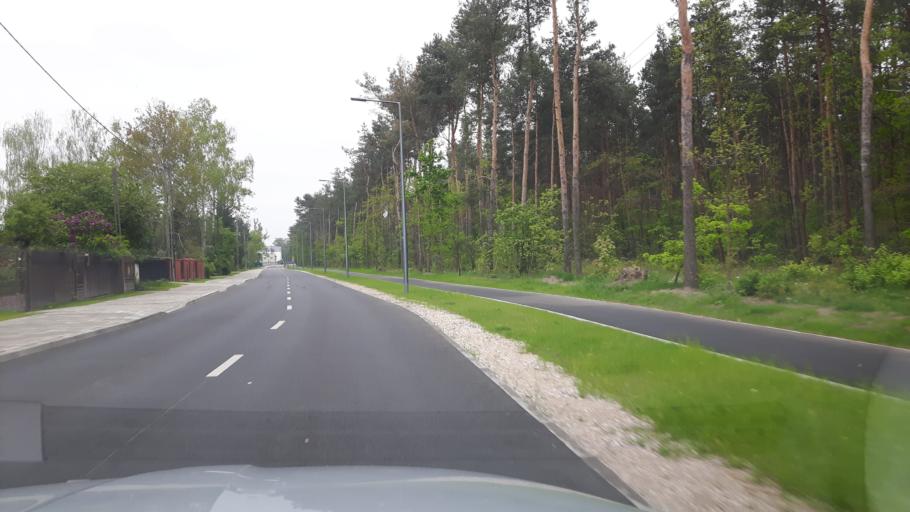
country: PL
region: Masovian Voivodeship
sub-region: Warszawa
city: Rembertow
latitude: 52.2646
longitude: 21.1488
